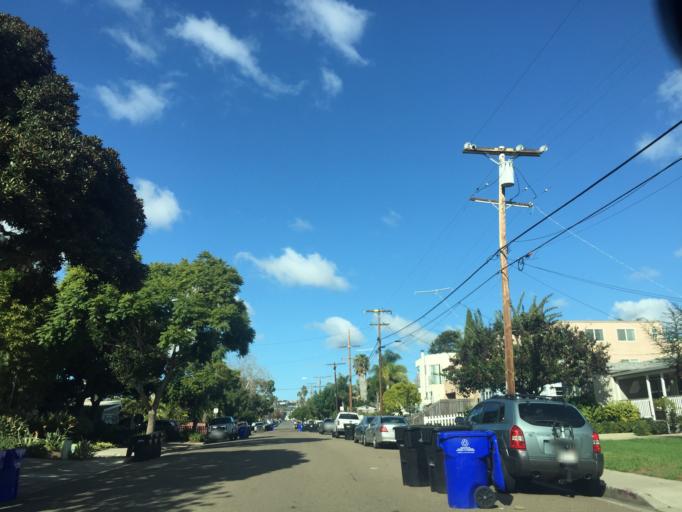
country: US
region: California
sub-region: San Diego County
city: La Jolla
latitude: 32.7915
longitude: -117.2422
